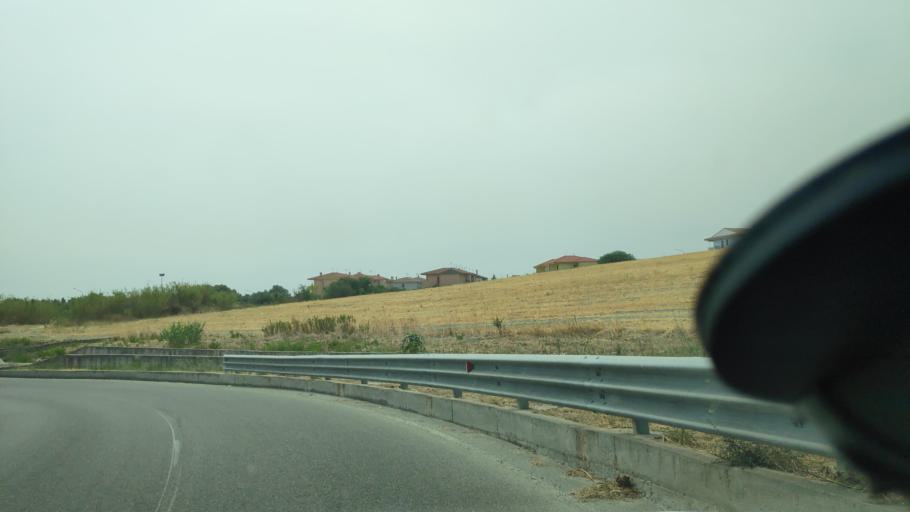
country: IT
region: Calabria
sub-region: Provincia di Catanzaro
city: Sant'Andrea Ionio Marina
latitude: 38.6170
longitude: 16.5523
